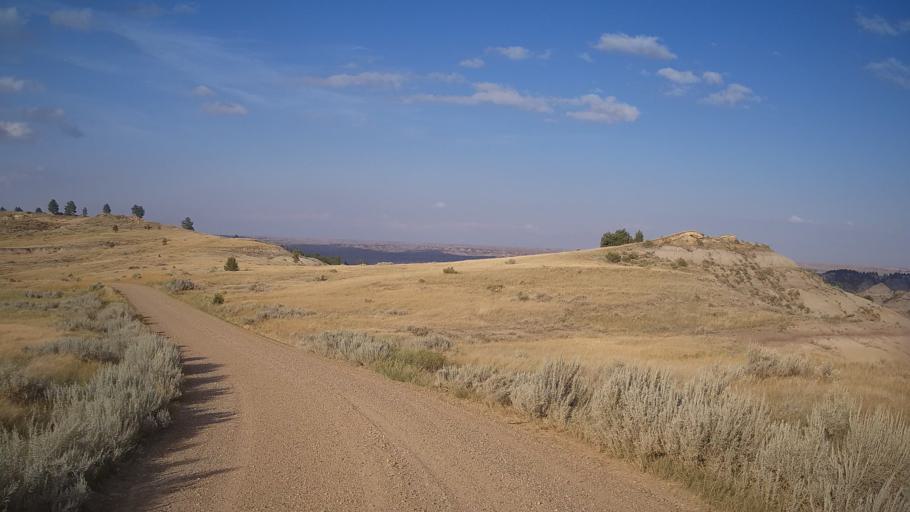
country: US
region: Montana
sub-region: Dawson County
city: Glendive
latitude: 47.0531
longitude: -104.6729
